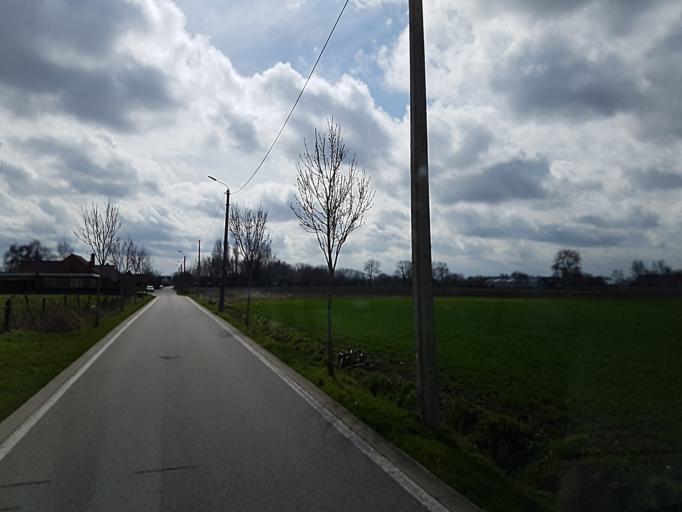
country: BE
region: Flanders
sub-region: Provincie Oost-Vlaanderen
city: Deinze
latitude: 50.9470
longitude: 3.4952
